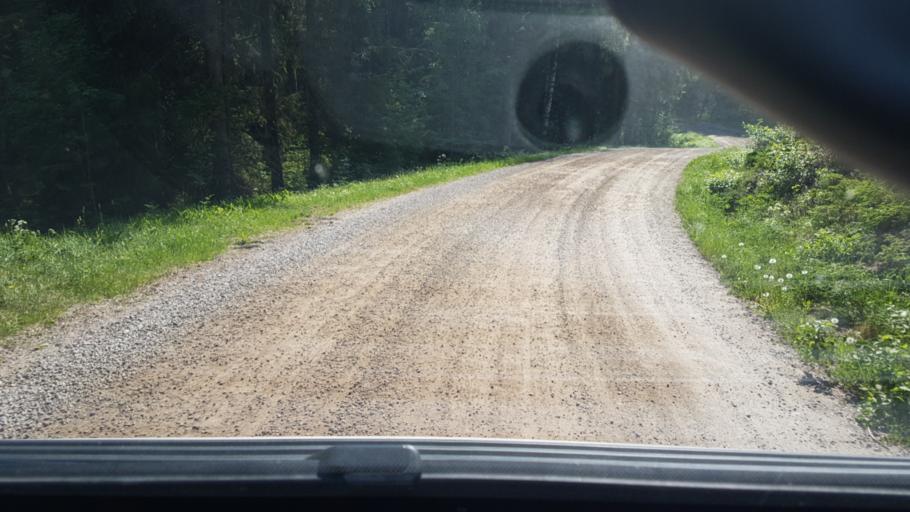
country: SE
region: Vaermland
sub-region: Eda Kommun
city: Amotfors
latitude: 59.8102
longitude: 12.4171
